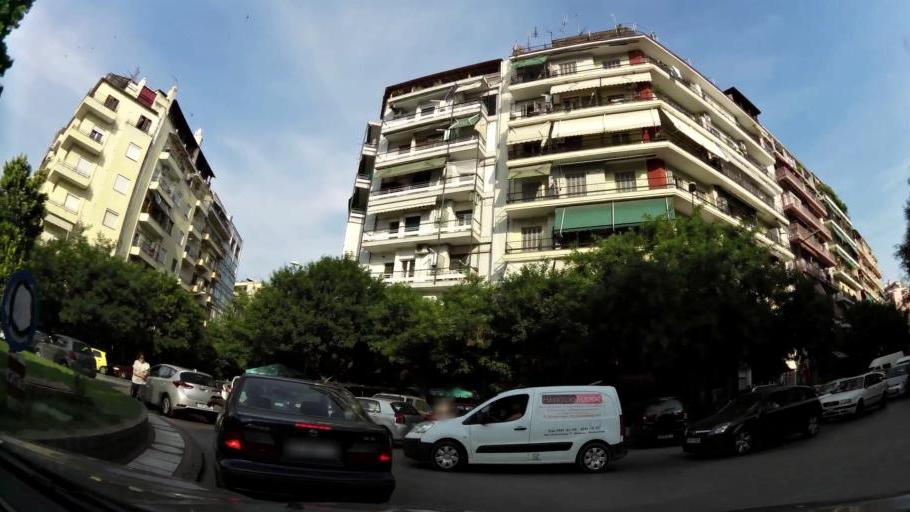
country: GR
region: Central Macedonia
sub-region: Nomos Thessalonikis
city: Thessaloniki
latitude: 40.6405
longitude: 22.9404
